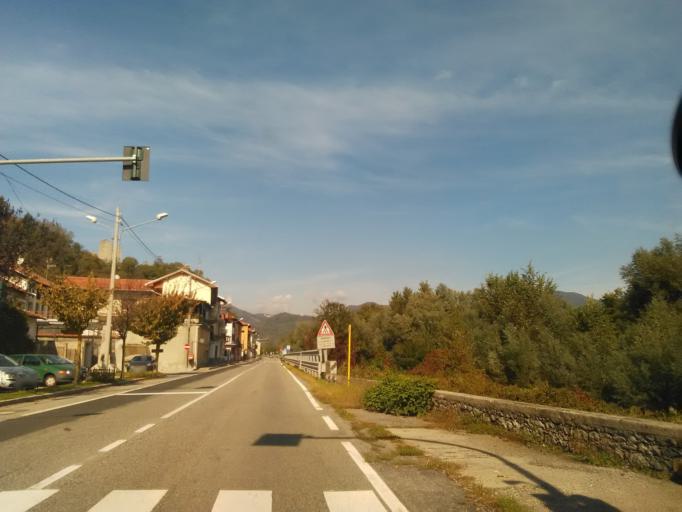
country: IT
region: Piedmont
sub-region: Provincia di Novara
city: Grignasco
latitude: 45.6651
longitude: 8.3327
